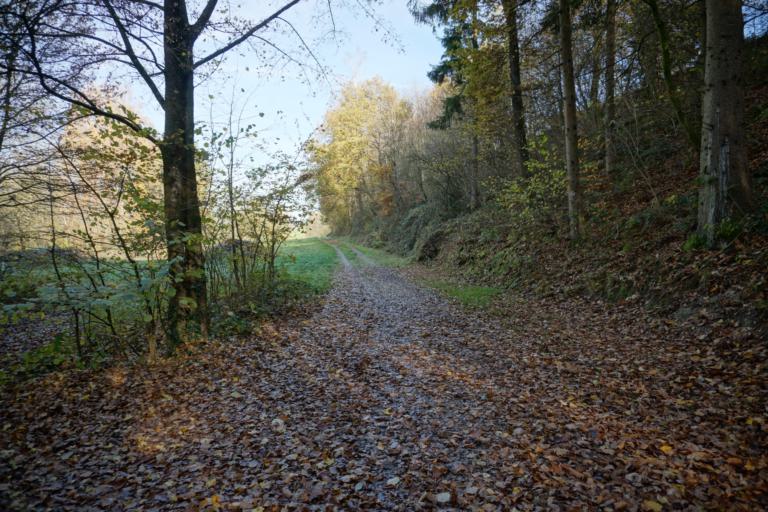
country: DE
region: Baden-Wuerttemberg
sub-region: Karlsruhe Region
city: Neunkirchen
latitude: 49.3612
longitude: 9.0136
